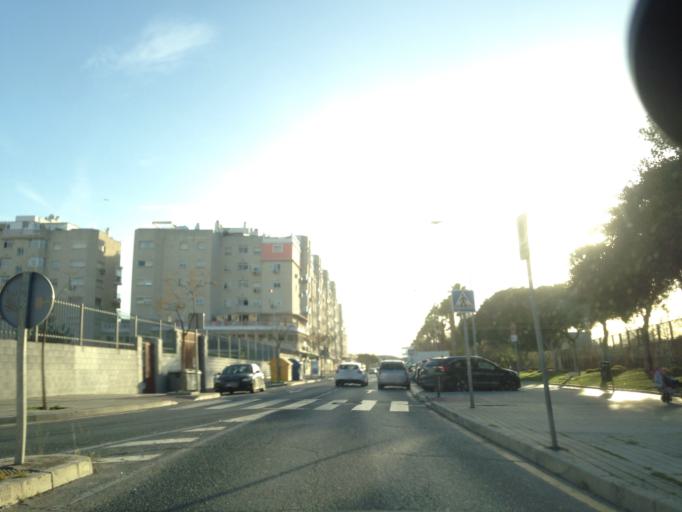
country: ES
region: Andalusia
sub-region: Provincia de Malaga
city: Malaga
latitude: 36.6949
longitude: -4.4568
